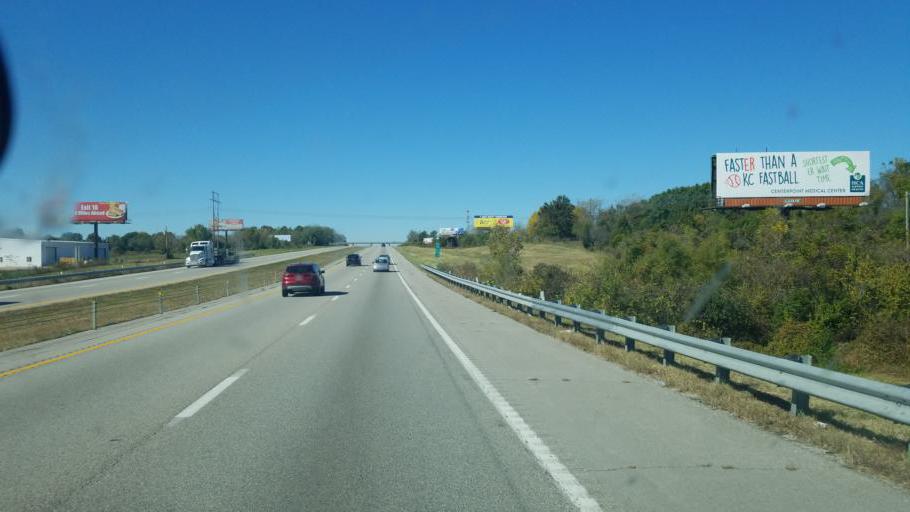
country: US
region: Missouri
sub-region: Jackson County
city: Oak Grove
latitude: 39.0178
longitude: -94.1611
